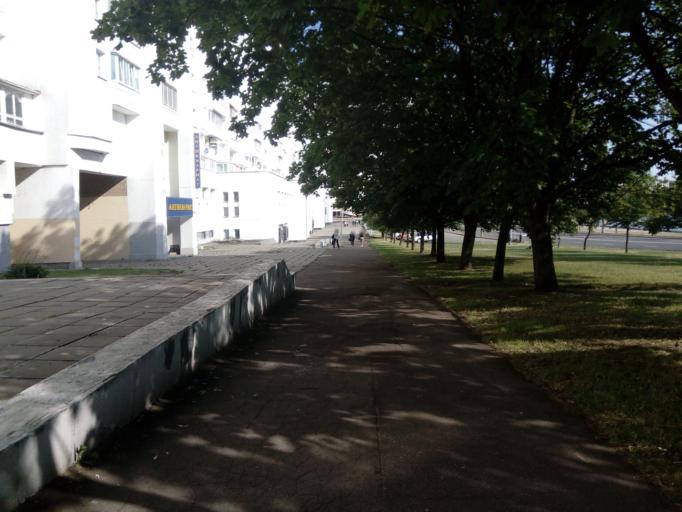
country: BY
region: Minsk
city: Minsk
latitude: 53.9132
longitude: 27.5548
